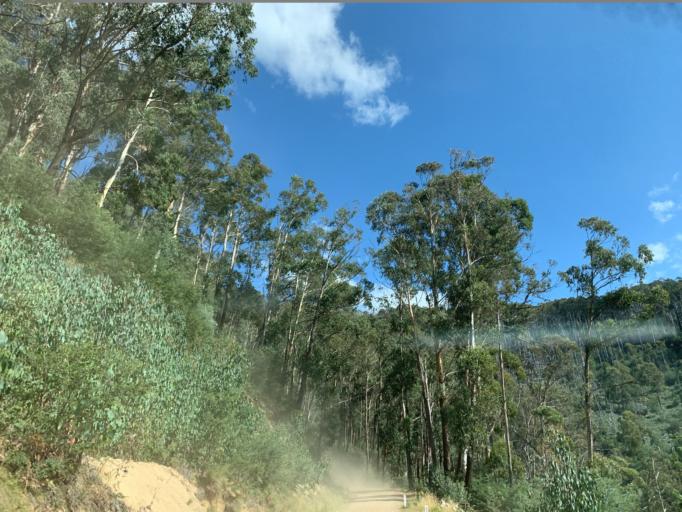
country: AU
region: Victoria
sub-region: Mansfield
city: Mansfield
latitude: -37.0993
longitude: 146.4835
